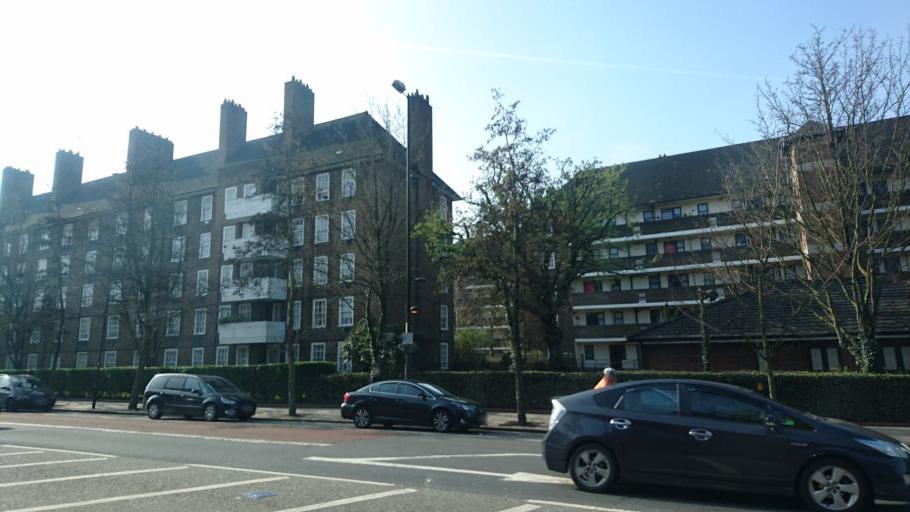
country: GB
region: England
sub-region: Greater London
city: Holloway
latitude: 51.5548
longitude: -0.1154
